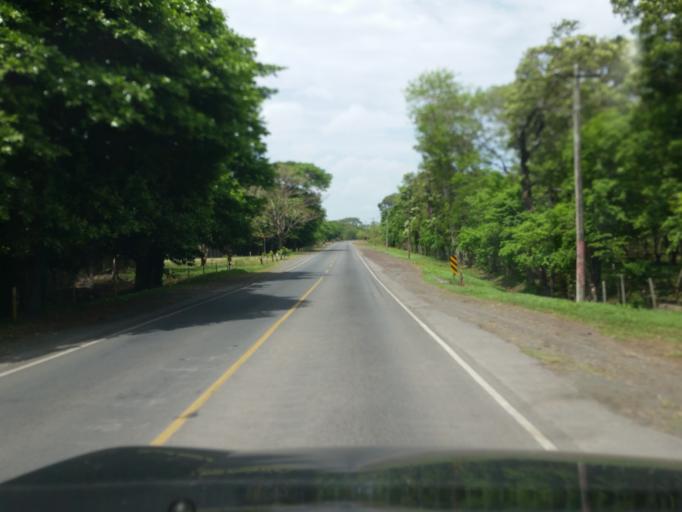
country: NI
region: Granada
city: Nandaime
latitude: 11.7839
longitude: -86.0498
